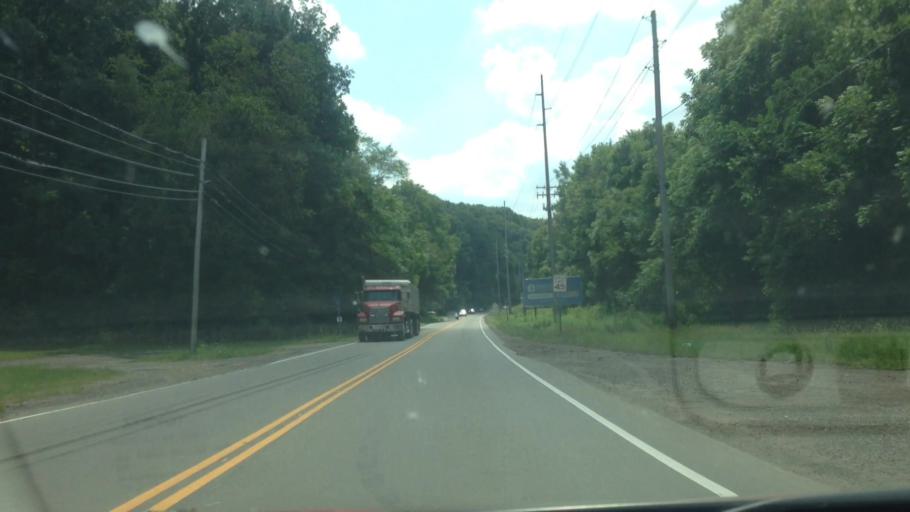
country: US
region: Ohio
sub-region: Stark County
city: Massillon
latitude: 40.8402
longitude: -81.5224
